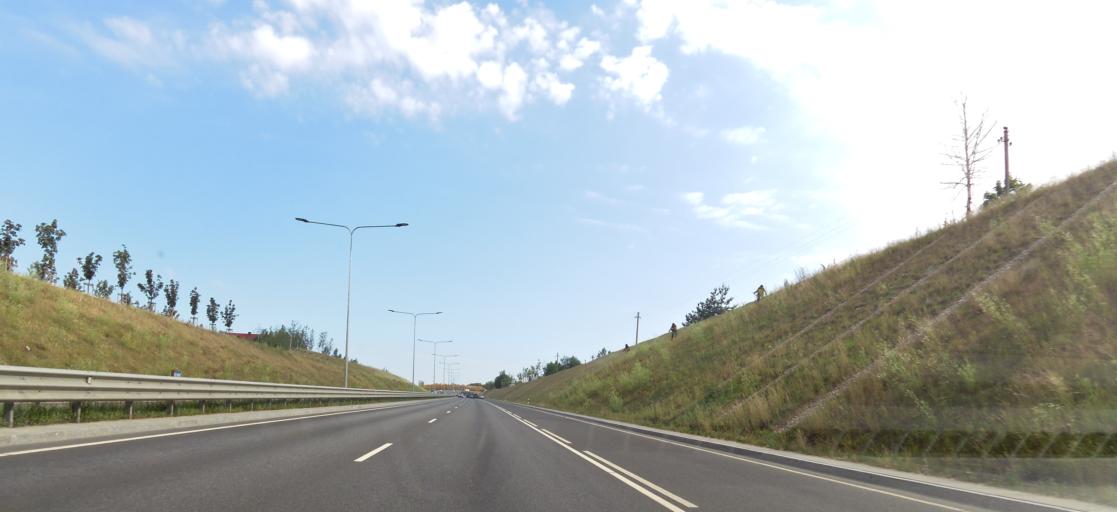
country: LT
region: Vilnius County
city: Pasilaiciai
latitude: 54.7281
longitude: 25.2081
